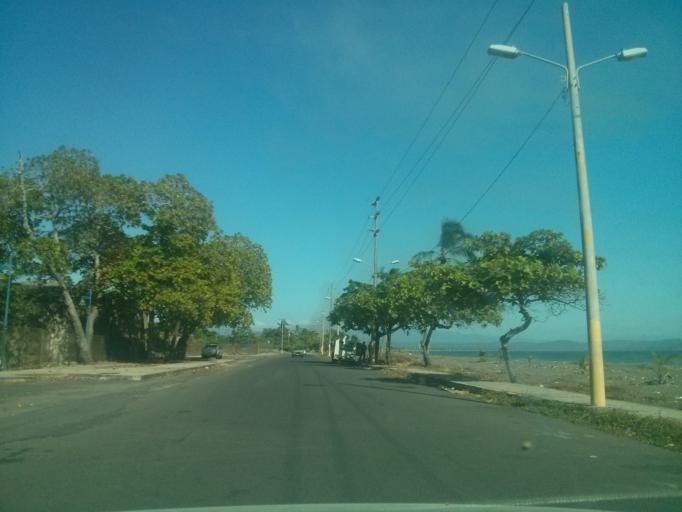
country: CR
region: Puntarenas
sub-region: Canton Central de Puntarenas
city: Puntarenas
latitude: 9.9770
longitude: -84.8265
